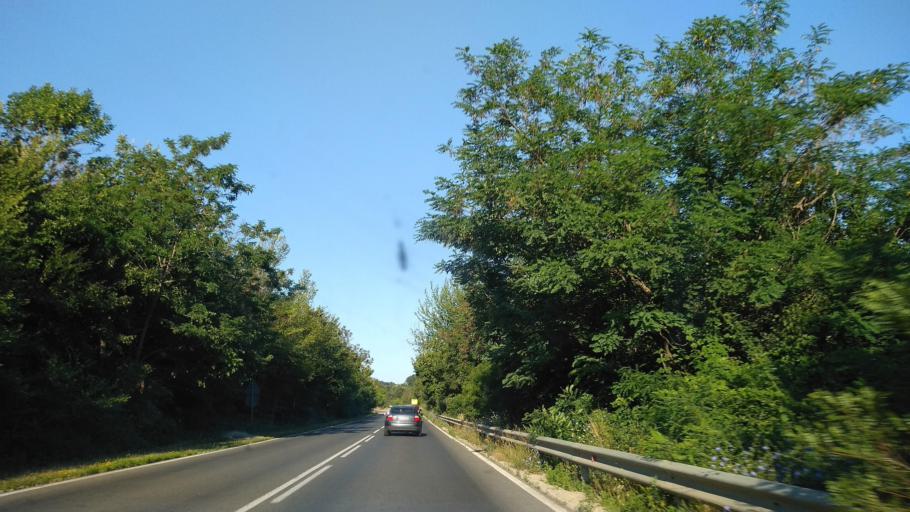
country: BG
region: Veliko Turnovo
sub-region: Obshtina Pavlikeni
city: Byala Cherkva
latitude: 43.0661
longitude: 25.2965
